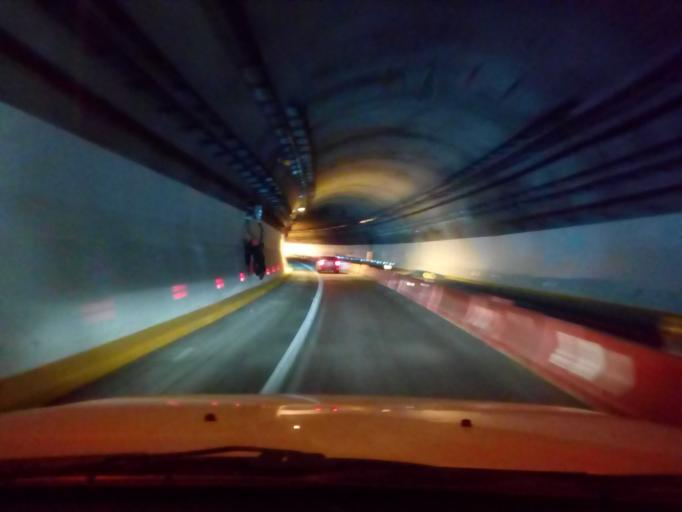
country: MX
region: Durango
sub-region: Pueblo Nuevo
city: La Ciudad
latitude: 23.5113
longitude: -105.8028
